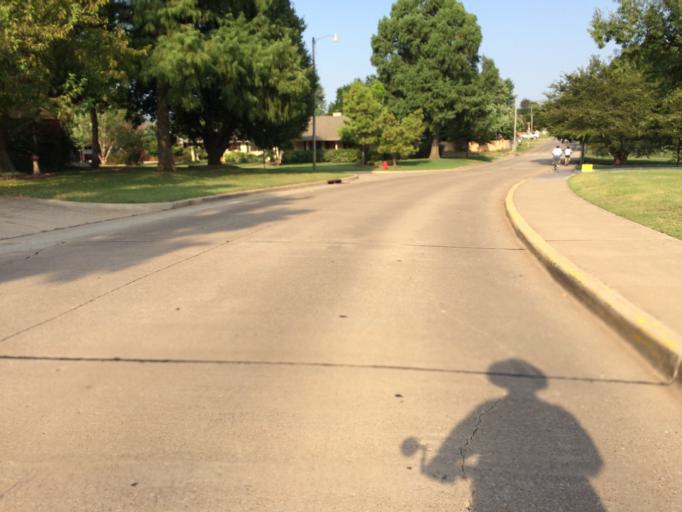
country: US
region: Oklahoma
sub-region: Cleveland County
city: Norman
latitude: 35.2242
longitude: -97.4695
